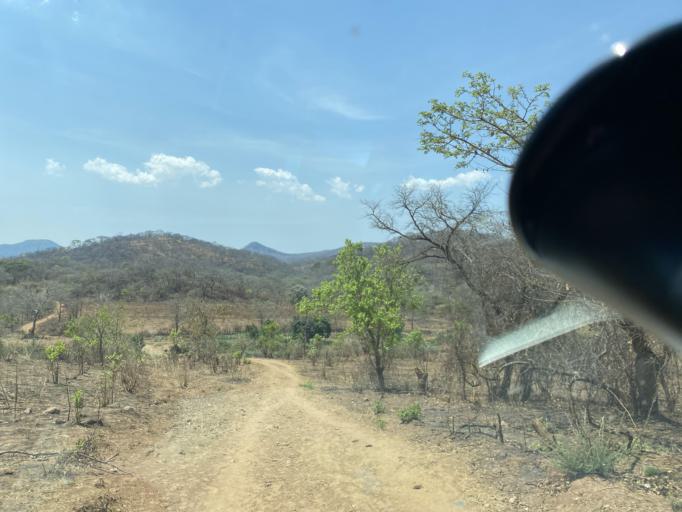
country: ZM
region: Lusaka
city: Kafue
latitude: -15.7870
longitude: 28.4605
